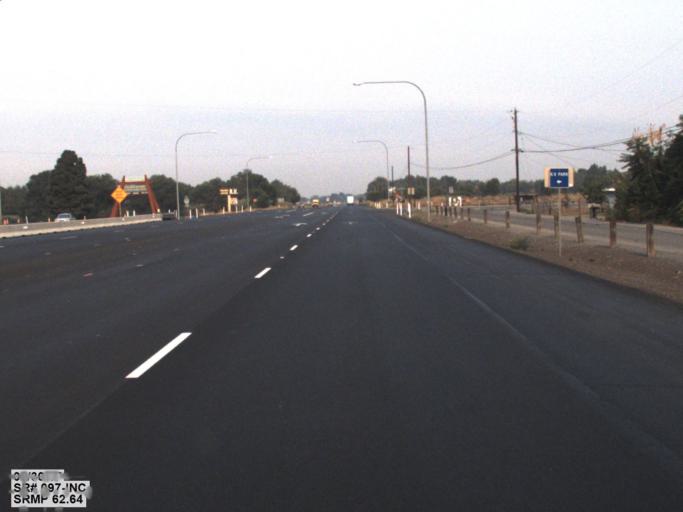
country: US
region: Washington
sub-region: Yakima County
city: Toppenish
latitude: 46.3803
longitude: -120.3397
